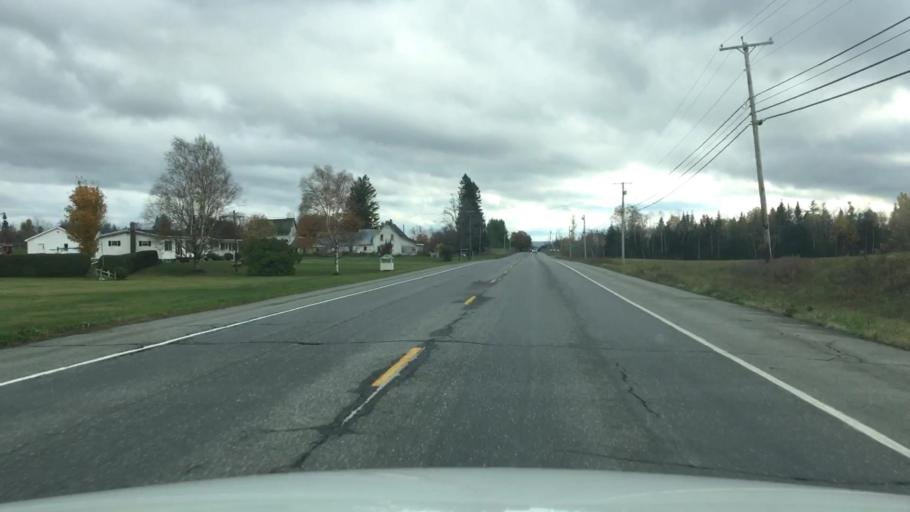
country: US
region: Maine
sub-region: Aroostook County
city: Houlton
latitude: 46.1869
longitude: -67.8412
